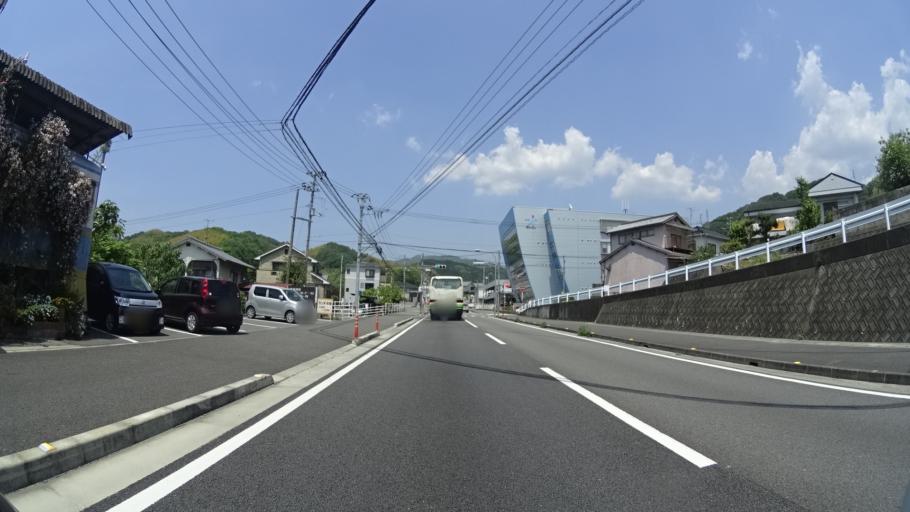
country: JP
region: Ehime
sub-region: Shikoku-chuo Shi
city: Matsuyama
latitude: 33.8536
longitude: 132.8097
